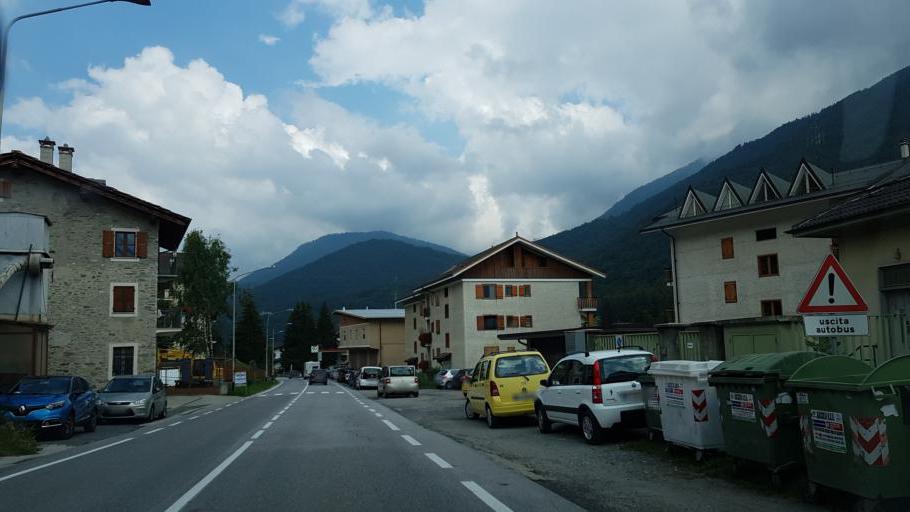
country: IT
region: Piedmont
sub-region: Provincia di Cuneo
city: Sampeyre
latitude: 44.5796
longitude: 7.1831
